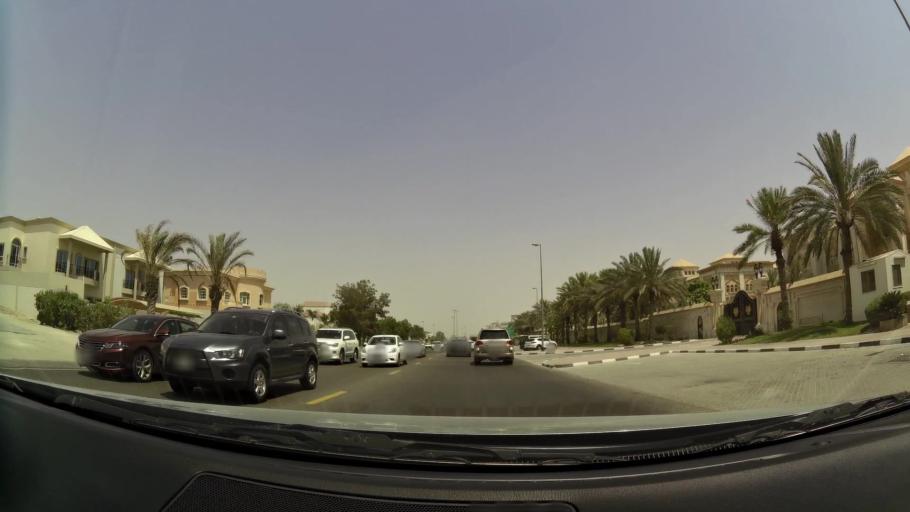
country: AE
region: Dubai
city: Dubai
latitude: 25.1417
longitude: 55.2021
